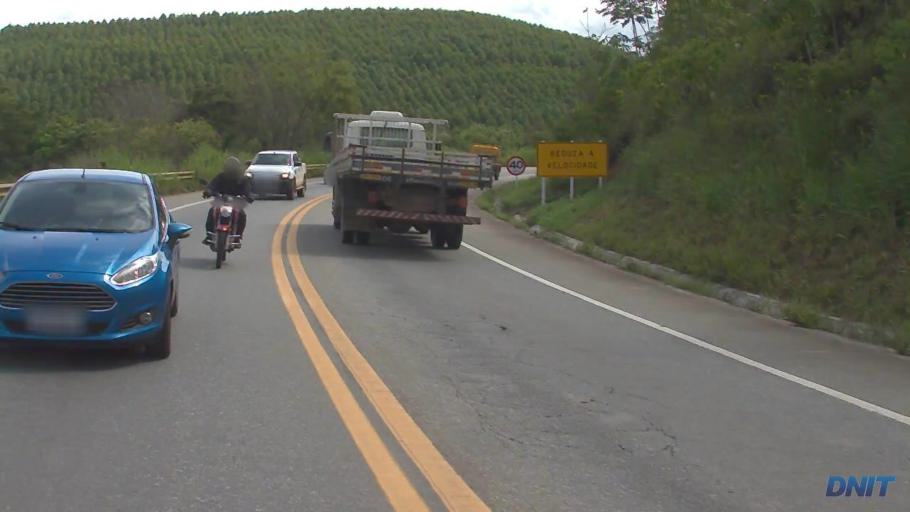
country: BR
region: Minas Gerais
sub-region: Ipaba
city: Ipaba
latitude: -19.3606
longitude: -42.4470
